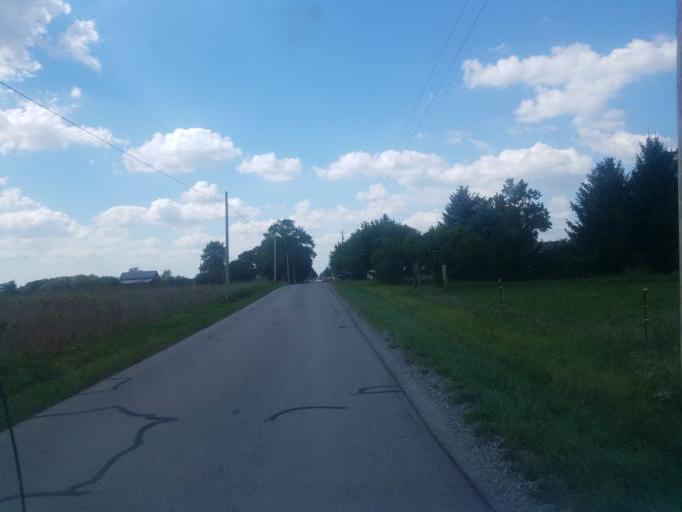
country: US
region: Ohio
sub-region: Logan County
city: Lakeview
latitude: 40.6516
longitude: -83.9570
